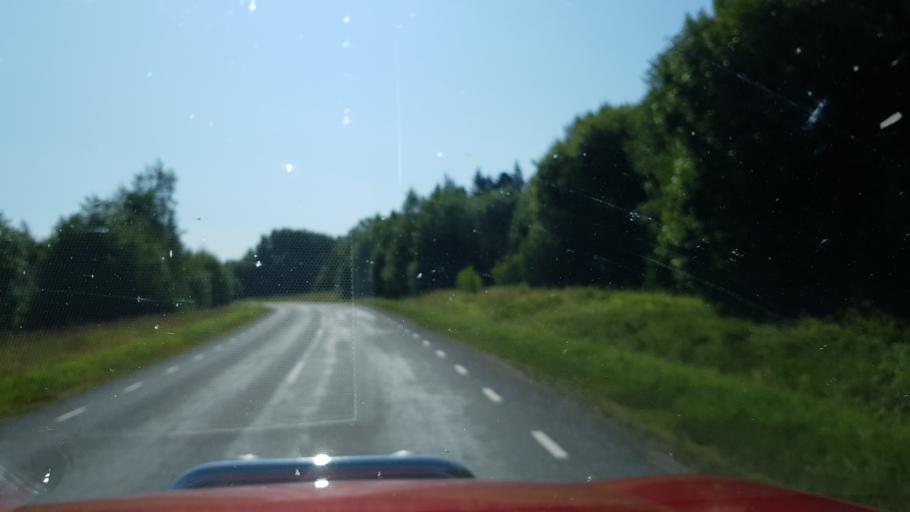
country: EE
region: Vorumaa
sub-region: Voru linn
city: Voru
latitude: 57.9748
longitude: 26.8276
